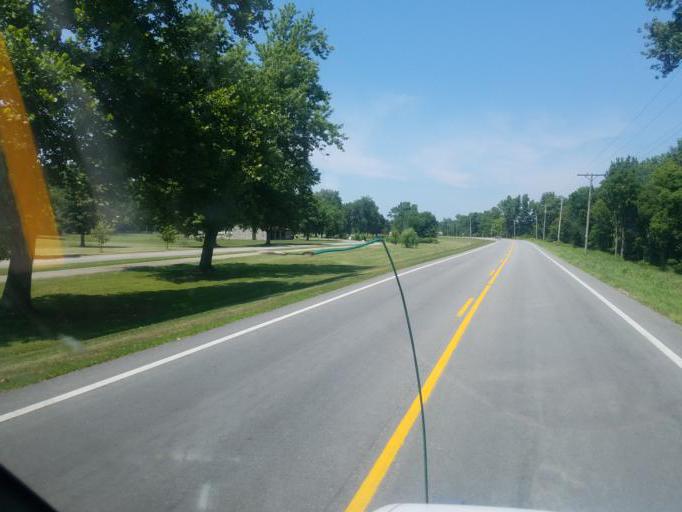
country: US
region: Ohio
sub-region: Auglaize County
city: Saint Marys
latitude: 40.5369
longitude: -84.4164
